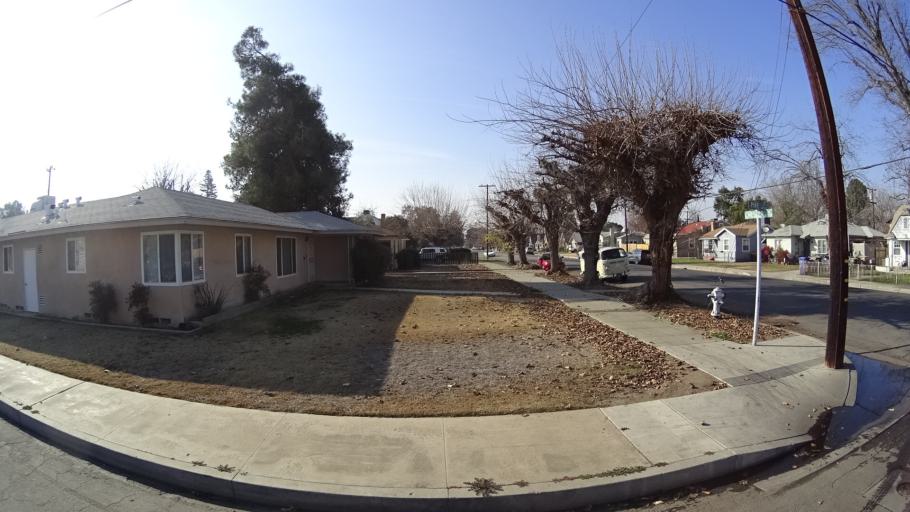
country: US
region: California
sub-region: Kern County
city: Bakersfield
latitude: 35.3648
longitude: -119.0317
